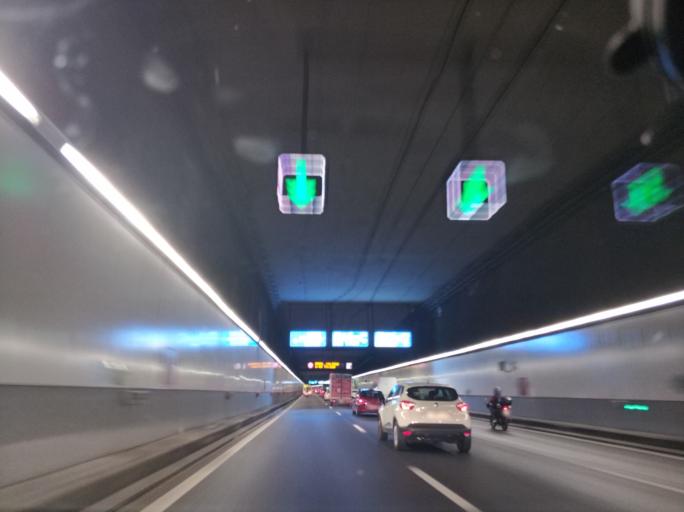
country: ES
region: Madrid
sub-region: Provincia de Madrid
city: Usera
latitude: 40.3907
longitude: -3.6997
